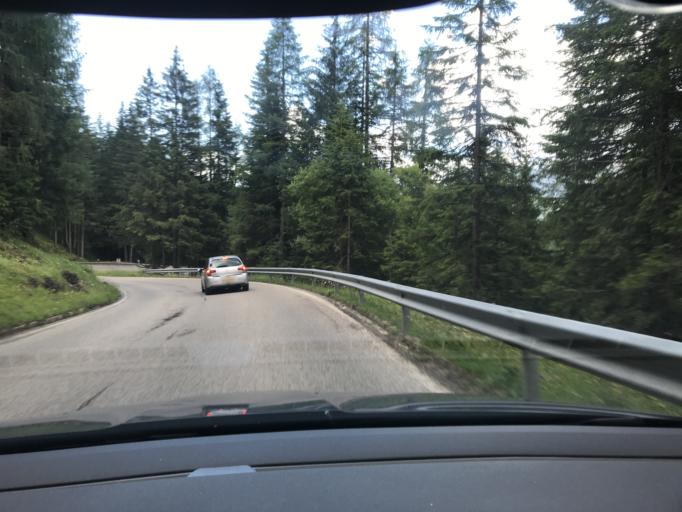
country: IT
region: Veneto
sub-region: Provincia di Belluno
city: Livinallongo del Col di Lana
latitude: 46.4972
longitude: 11.9901
